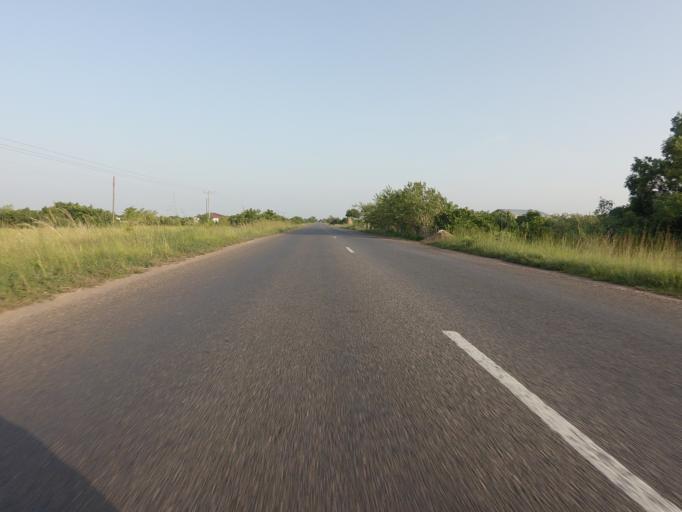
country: GH
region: Volta
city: Anloga
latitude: 6.0030
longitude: 0.6704
